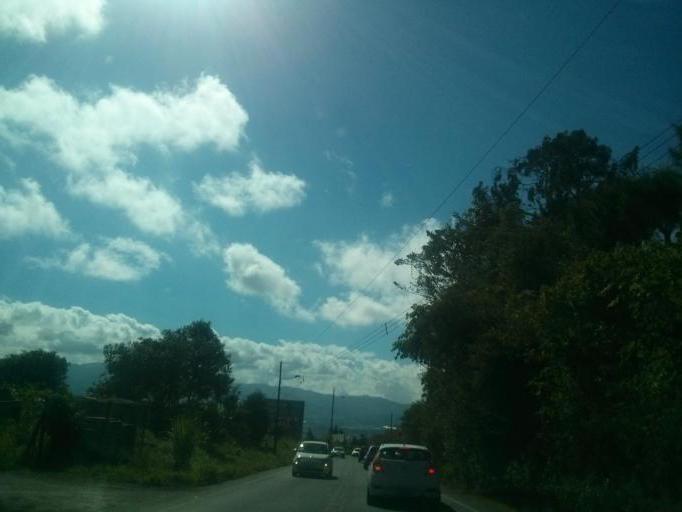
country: CR
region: Cartago
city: Cot
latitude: 9.8846
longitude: -83.8876
